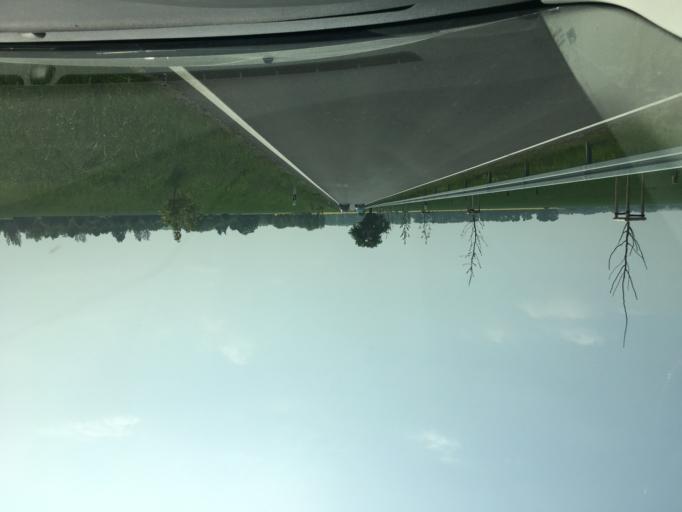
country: DE
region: Saxony
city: Grossposna
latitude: 51.3033
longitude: 12.4721
